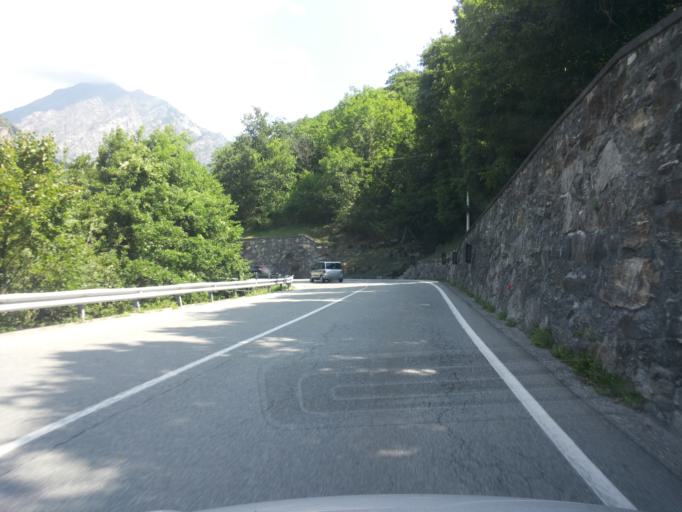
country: IT
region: Aosta Valley
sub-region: Valle d'Aosta
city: Perloz
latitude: 45.6035
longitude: 7.8069
